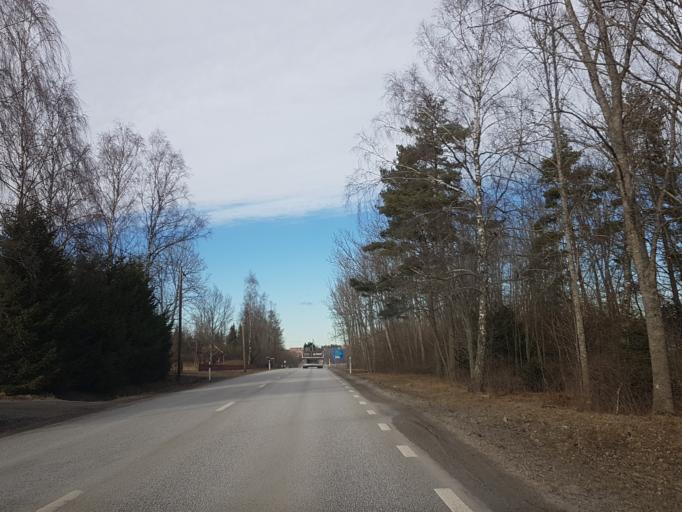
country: SE
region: Stockholm
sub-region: Norrtalje Kommun
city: Norrtalje
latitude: 59.7359
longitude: 18.6855
